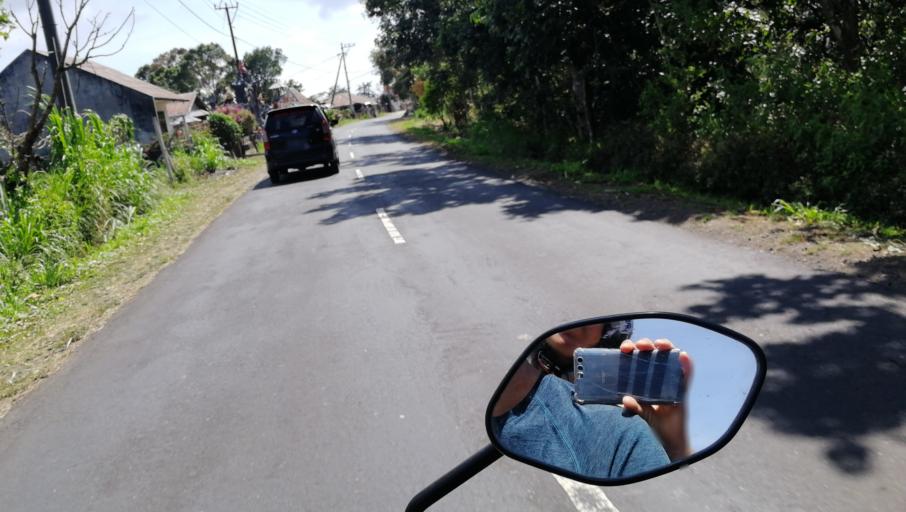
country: ID
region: Bali
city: Munduk
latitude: -8.2381
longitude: 115.1134
